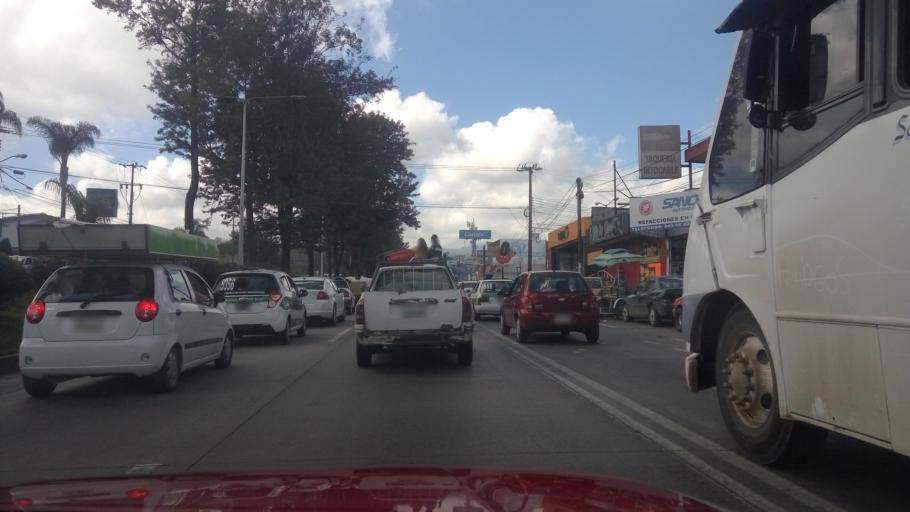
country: MX
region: Veracruz
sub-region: Xalapa
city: Xalapa de Enriquez
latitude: 19.5606
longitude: -96.9238
